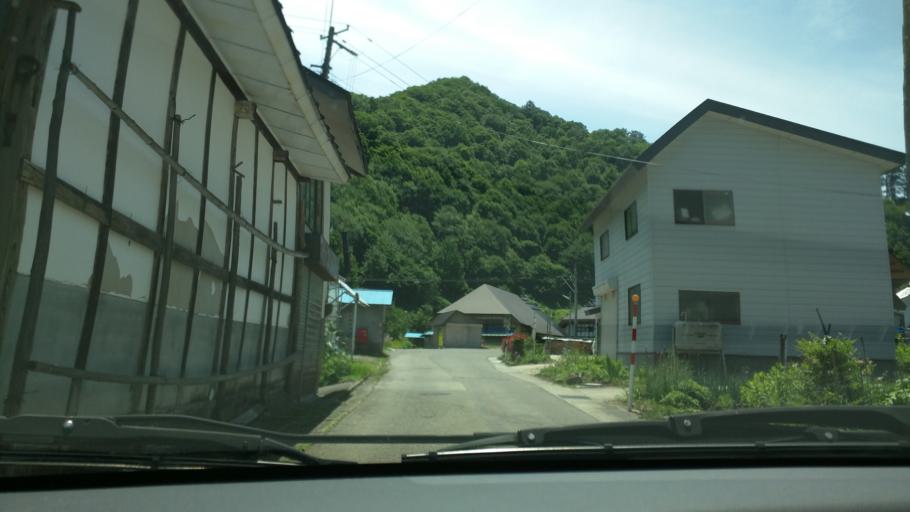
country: JP
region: Tochigi
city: Kuroiso
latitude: 37.2570
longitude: 139.7793
